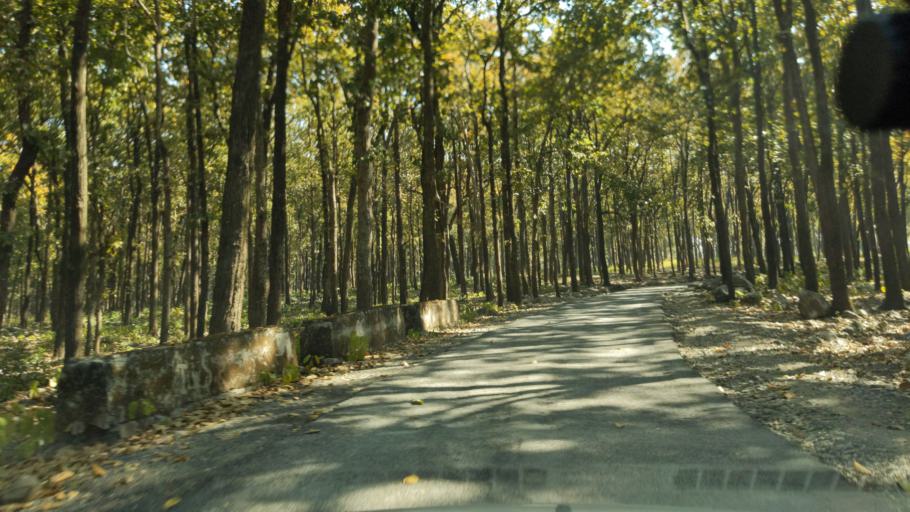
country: IN
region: Uttarakhand
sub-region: Naini Tal
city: Ramnagar
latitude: 29.4692
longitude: 79.2340
